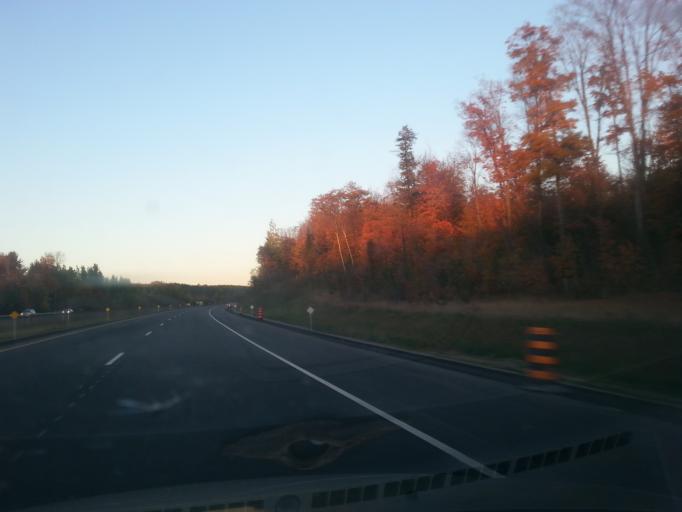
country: CA
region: Ontario
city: Barrie
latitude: 44.5622
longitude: -79.7358
